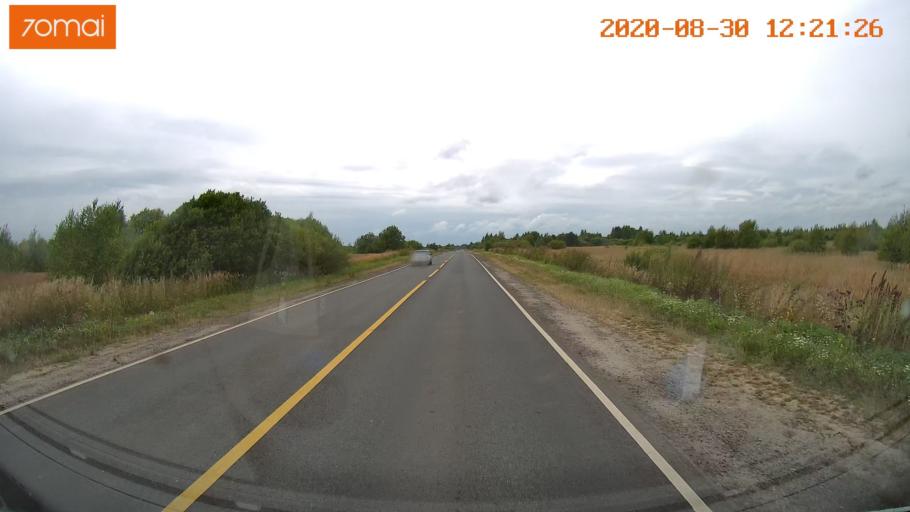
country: RU
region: Ivanovo
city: Yur'yevets
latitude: 57.3252
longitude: 42.8758
